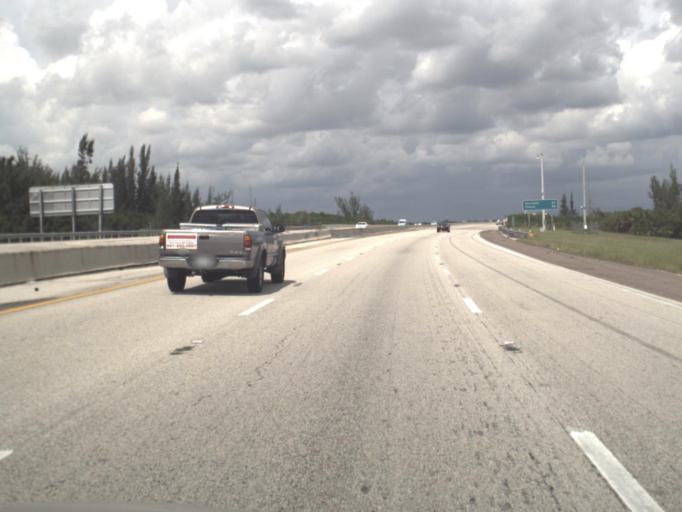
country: US
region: Florida
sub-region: Charlotte County
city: Punta Gorda
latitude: 26.9479
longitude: -82.0207
